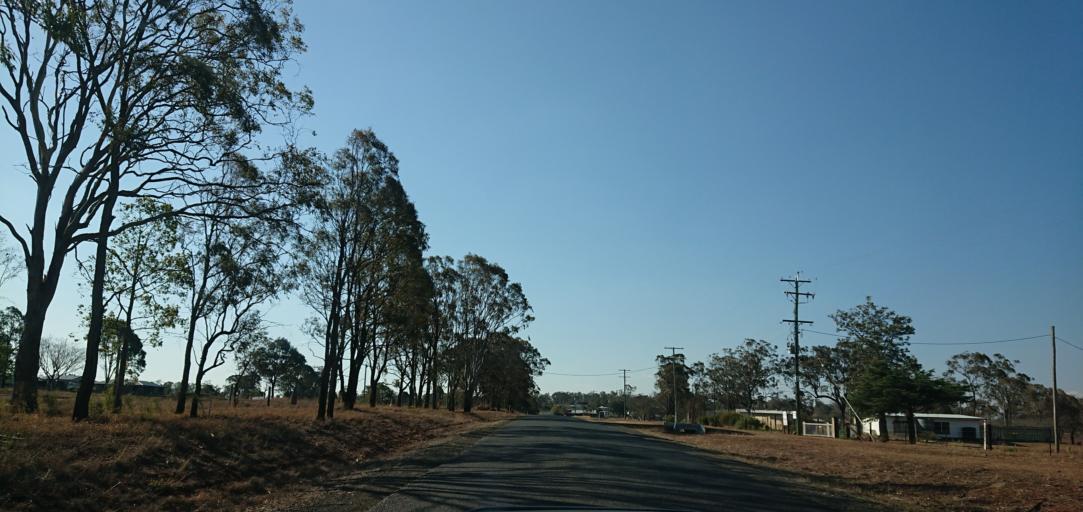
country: AU
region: Queensland
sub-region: Toowoomba
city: Westbrook
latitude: -27.6859
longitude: 151.7140
